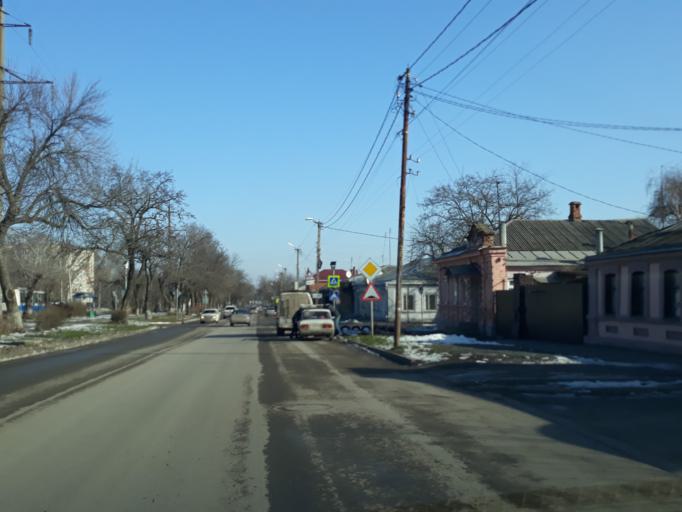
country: RU
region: Rostov
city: Taganrog
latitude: 47.2074
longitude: 38.9071
